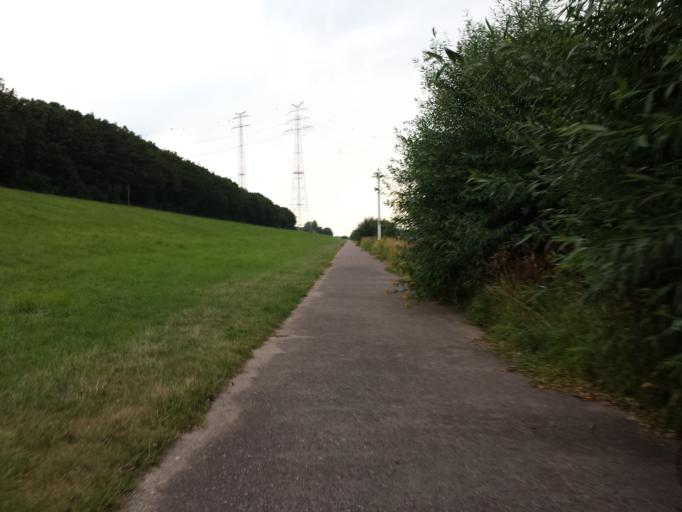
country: DE
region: Lower Saxony
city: Lemwerder
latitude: 53.1218
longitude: 8.6775
